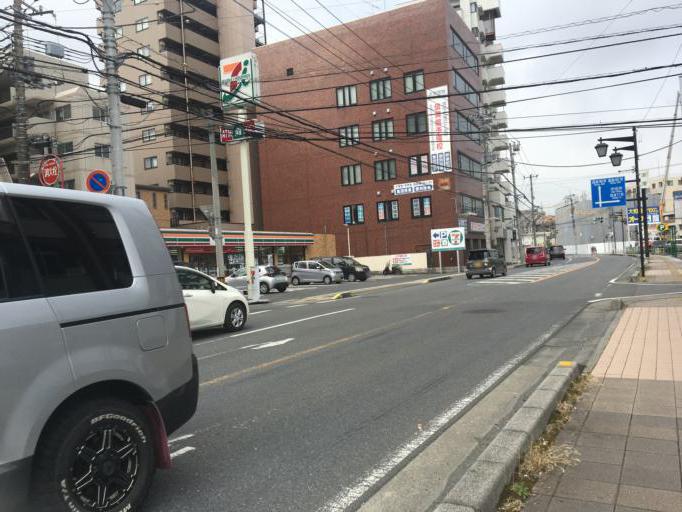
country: JP
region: Saitama
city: Kumagaya
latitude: 36.1386
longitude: 139.3870
